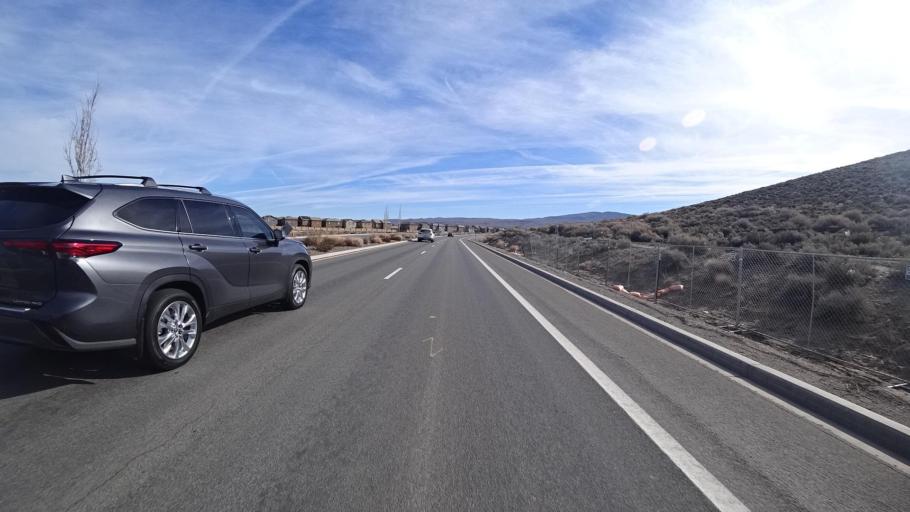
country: US
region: Nevada
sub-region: Washoe County
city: Spanish Springs
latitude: 39.6051
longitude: -119.7053
